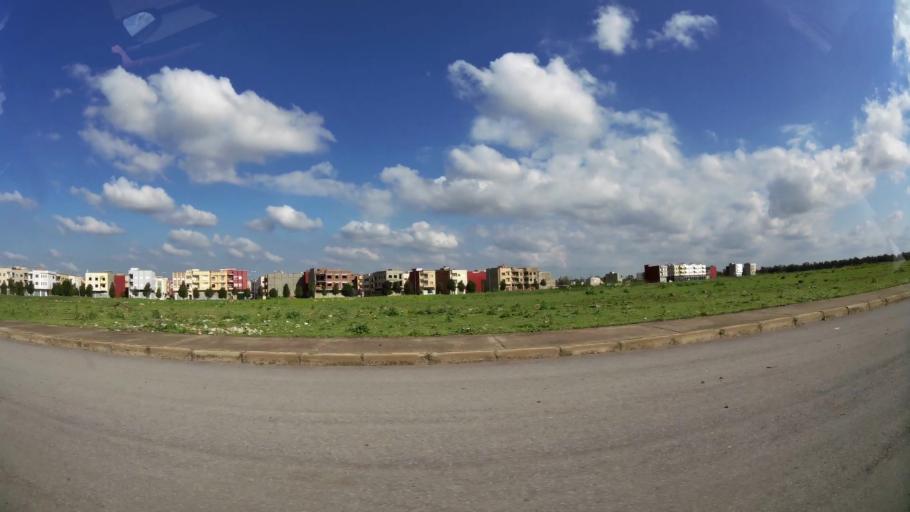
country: MA
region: Grand Casablanca
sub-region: Mediouna
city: Mediouna
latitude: 33.3874
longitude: -7.5496
